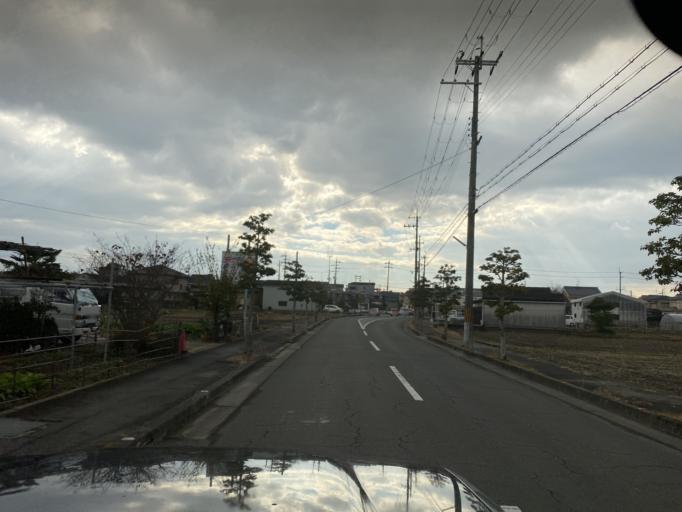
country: JP
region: Kyoto
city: Tanabe
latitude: 34.8421
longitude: 135.7803
